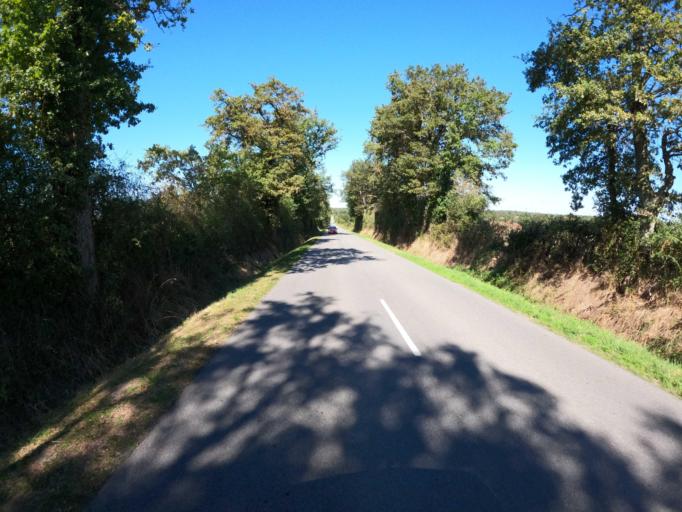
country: FR
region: Limousin
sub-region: Departement de la Haute-Vienne
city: Le Dorat
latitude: 46.2508
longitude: 1.0455
